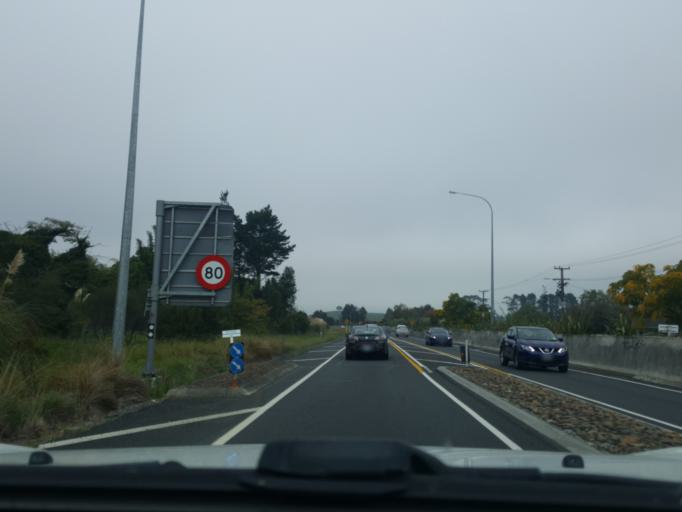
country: NZ
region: Waikato
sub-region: Waikato District
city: Ngaruawahia
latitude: -37.6129
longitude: 175.1945
